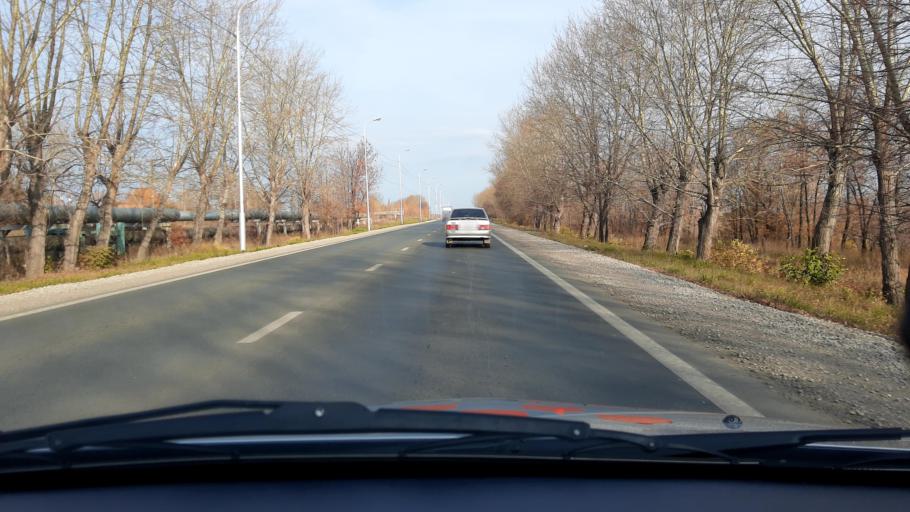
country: RU
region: Bashkortostan
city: Ufa
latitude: 54.8553
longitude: 56.1155
